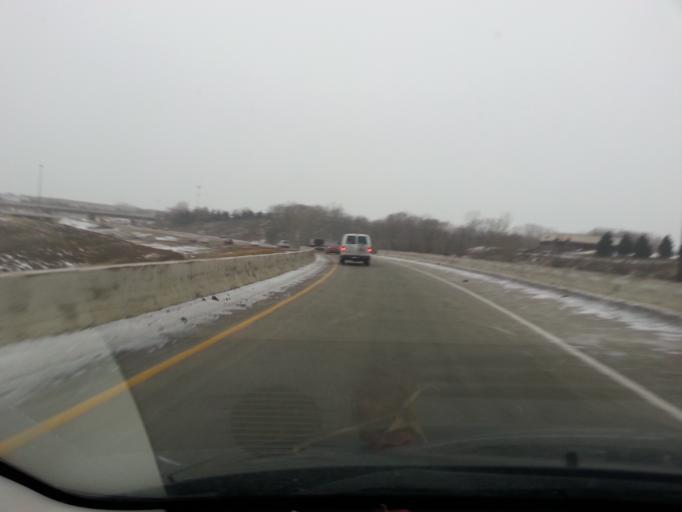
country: US
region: Minnesota
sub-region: Dakota County
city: Mendota Heights
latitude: 44.8647
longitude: -93.1448
